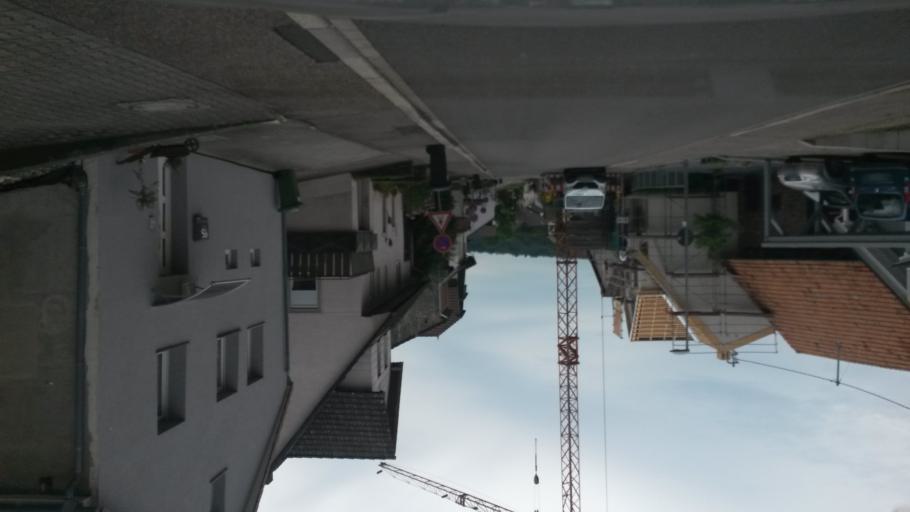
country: DE
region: Baden-Wuerttemberg
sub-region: Karlsruhe Region
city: Konigsbach-Stein
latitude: 48.9122
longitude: 8.5298
